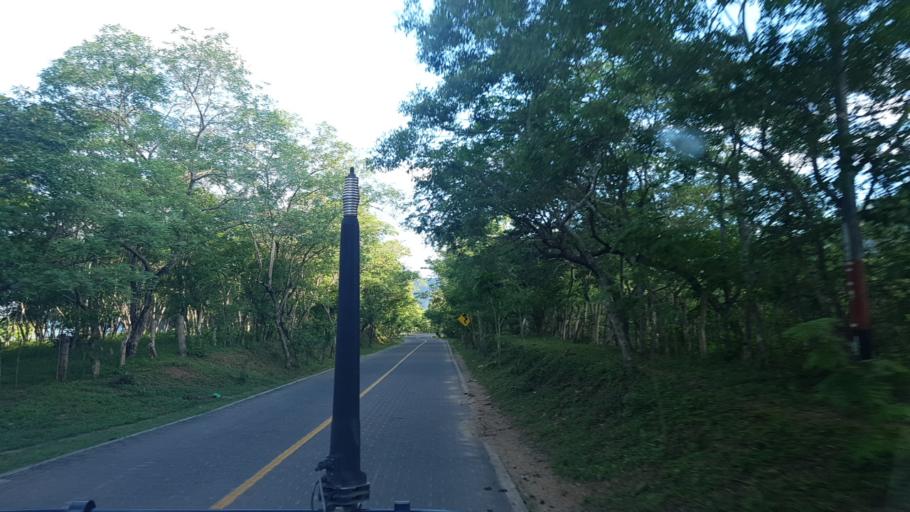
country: NI
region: Nueva Segovia
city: Ocotal
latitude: 13.6453
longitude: -86.6037
